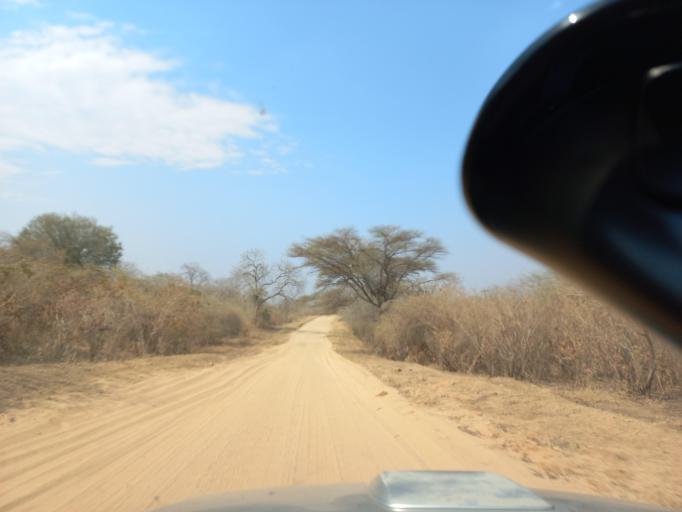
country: ZW
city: Chirundu
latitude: -15.9255
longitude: 28.8861
